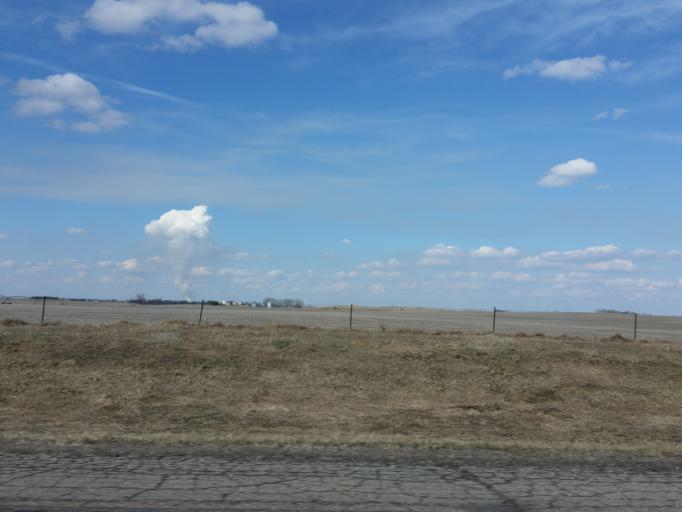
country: US
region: Minnesota
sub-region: Lac qui Parle County
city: Madison
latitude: 44.9357
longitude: -96.3651
